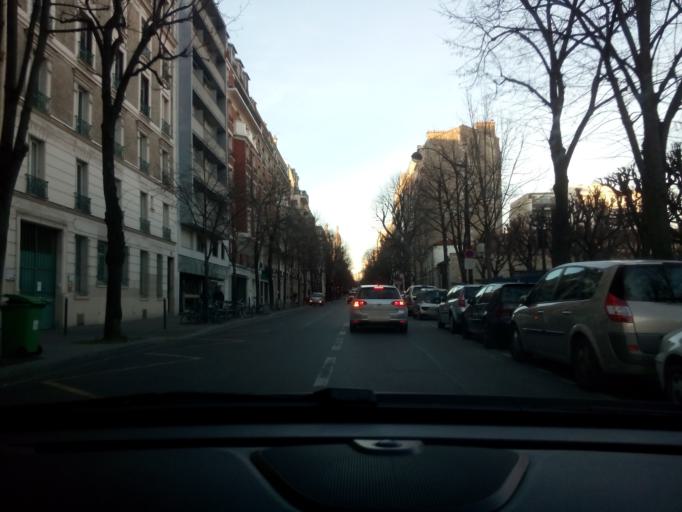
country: FR
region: Ile-de-France
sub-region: Departement du Val-de-Marne
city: Gentilly
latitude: 48.8224
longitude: 2.3476
